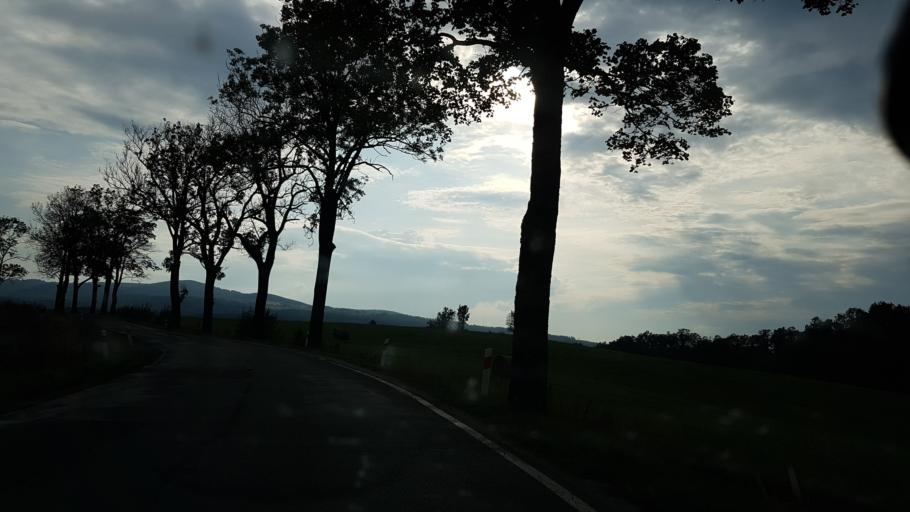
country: PL
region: Lower Silesian Voivodeship
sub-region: Powiat kamiennogorski
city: Marciszow
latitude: 50.8708
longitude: 15.9999
